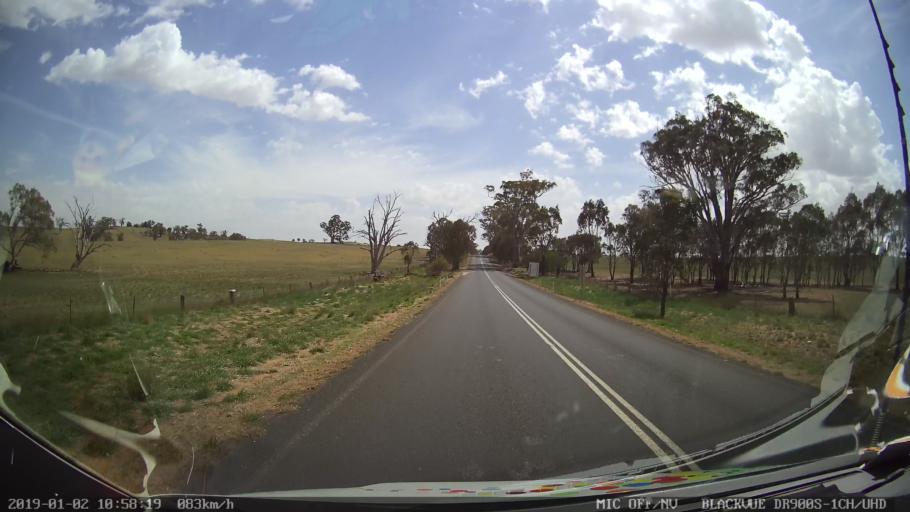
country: AU
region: New South Wales
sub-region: Cootamundra
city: Cootamundra
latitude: -34.6258
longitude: 148.2901
